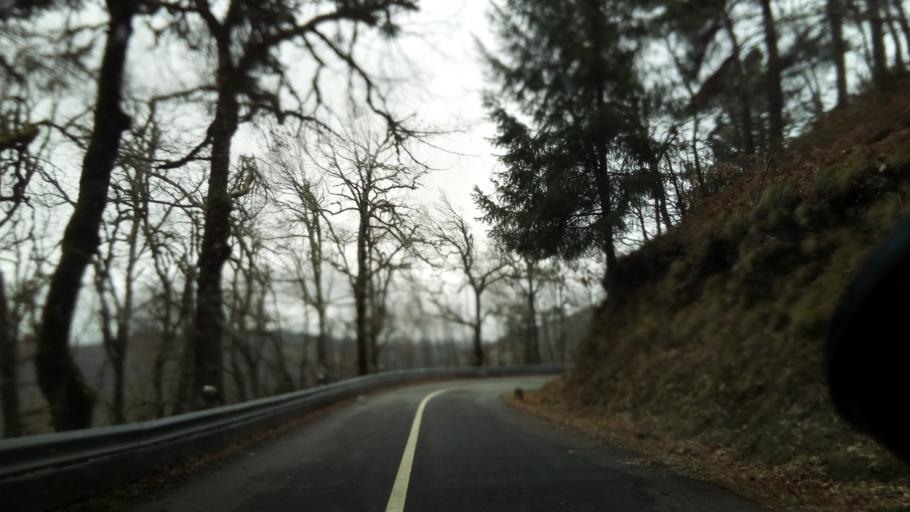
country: PT
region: Guarda
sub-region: Manteigas
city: Manteigas
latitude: 40.4126
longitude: -7.5507
